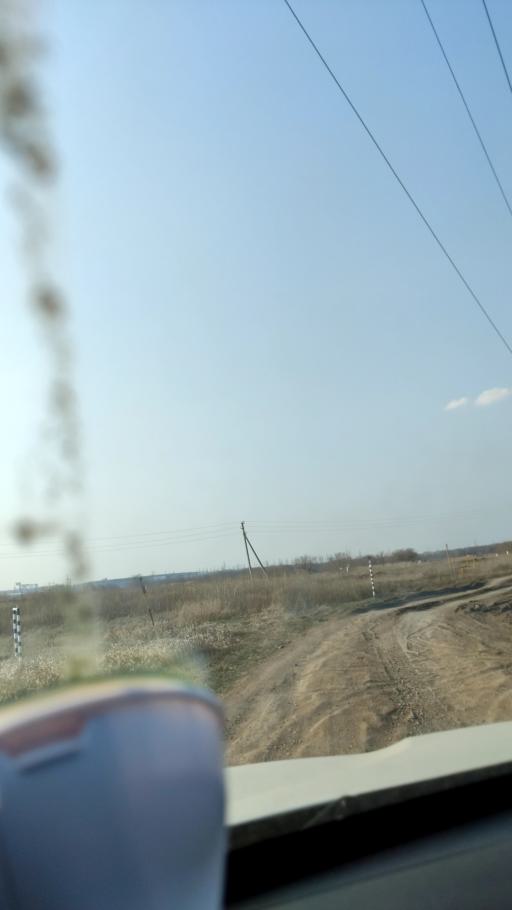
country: RU
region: Samara
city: Kinel'
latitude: 53.2551
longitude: 50.5293
